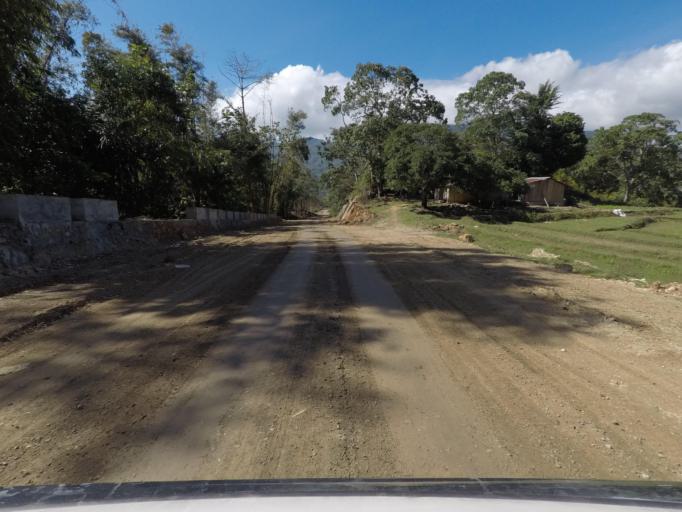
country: TL
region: Baucau
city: Venilale
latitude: -8.6598
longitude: 126.3698
